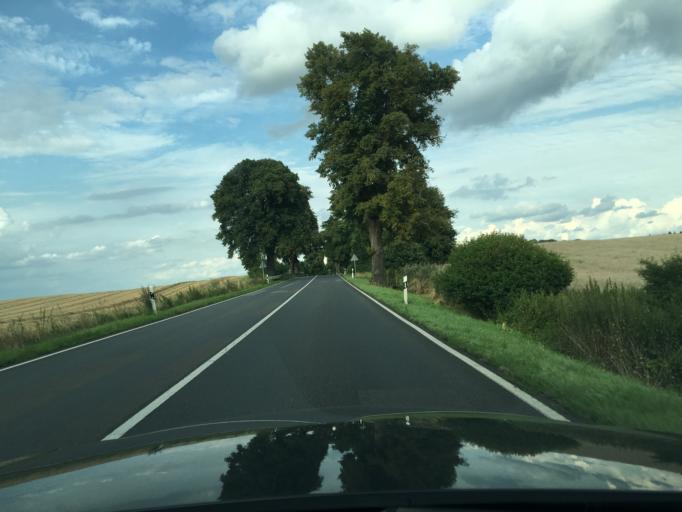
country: DE
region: Mecklenburg-Vorpommern
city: Wustrow
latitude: 53.4268
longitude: 13.1458
